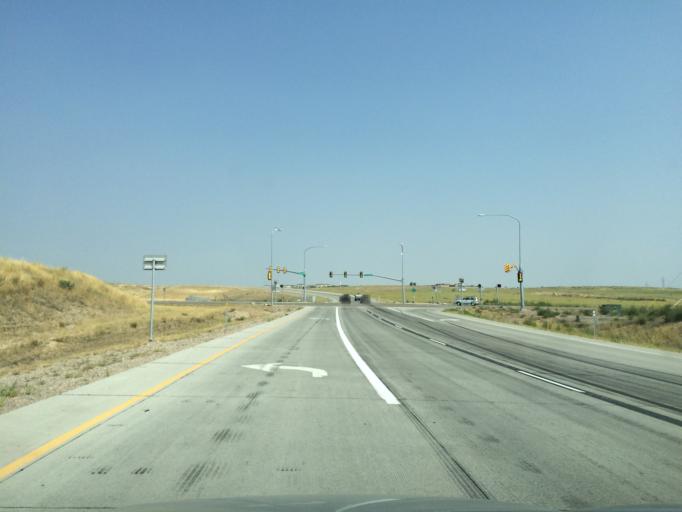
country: US
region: Utah
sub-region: Salt Lake County
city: Oquirrh
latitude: 40.6084
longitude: -112.0329
